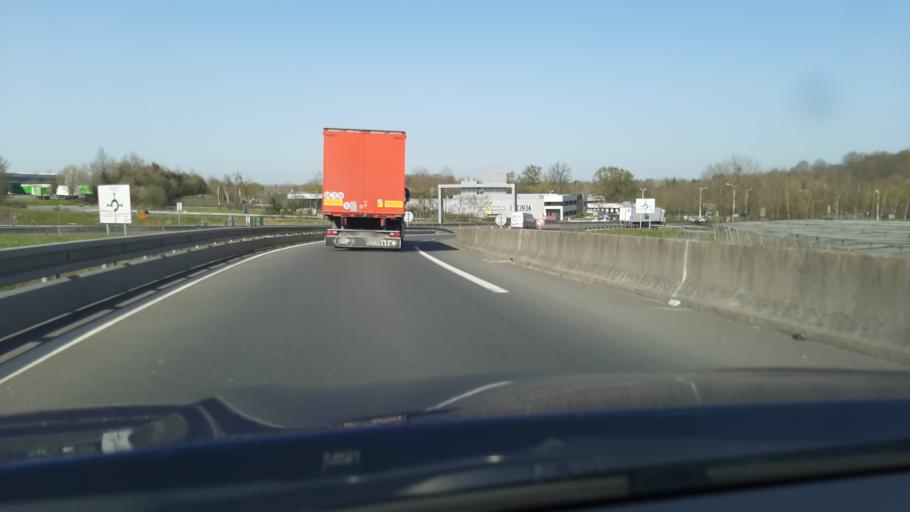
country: FR
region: Pays de la Loire
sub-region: Departement de Maine-et-Loire
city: Ecouflant
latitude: 47.5041
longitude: -0.5018
